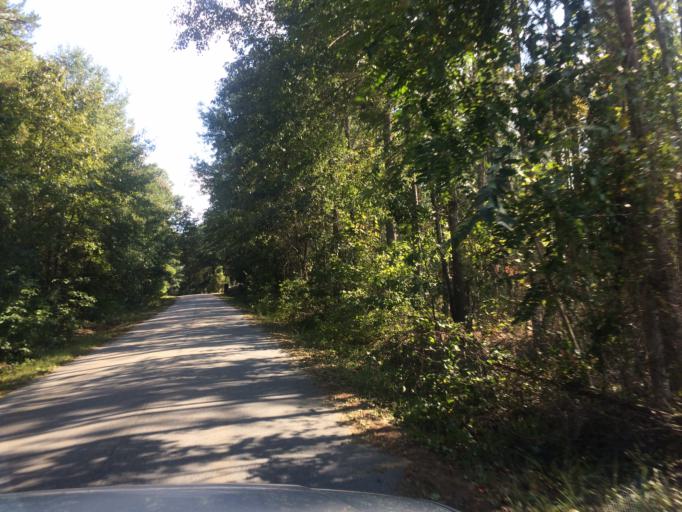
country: US
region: South Carolina
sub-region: Greenwood County
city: Ware Shoals
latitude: 34.4629
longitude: -82.1772
